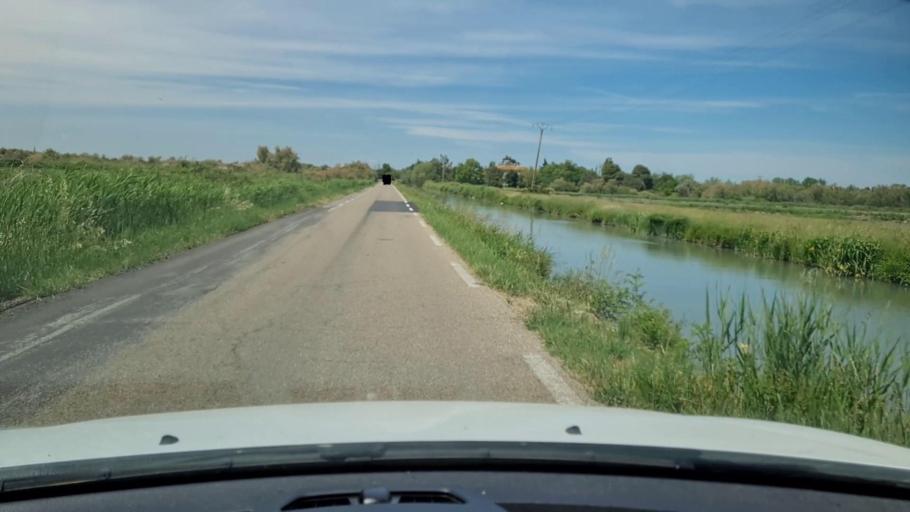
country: FR
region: Languedoc-Roussillon
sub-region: Departement du Gard
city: Vauvert
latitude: 43.6014
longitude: 4.3386
